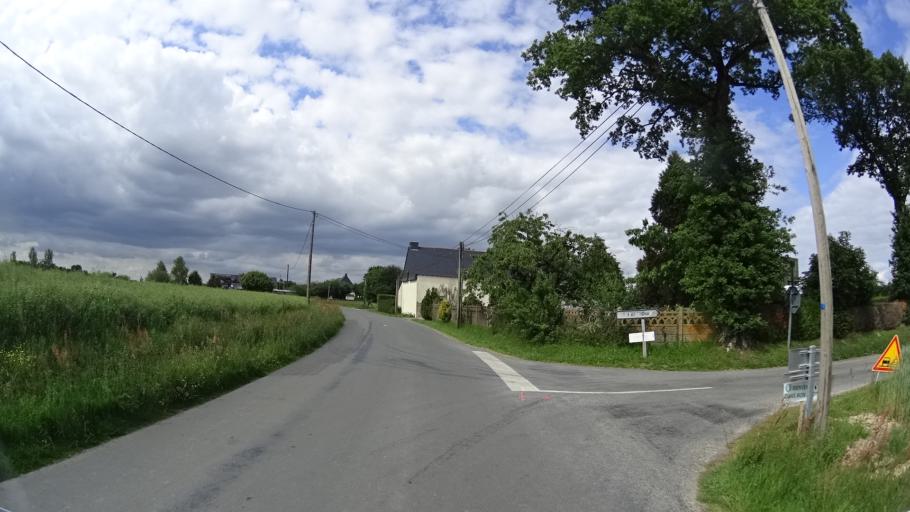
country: FR
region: Brittany
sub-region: Departement d'Ille-et-Vilaine
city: Iffendic
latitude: 48.0865
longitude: -2.0961
